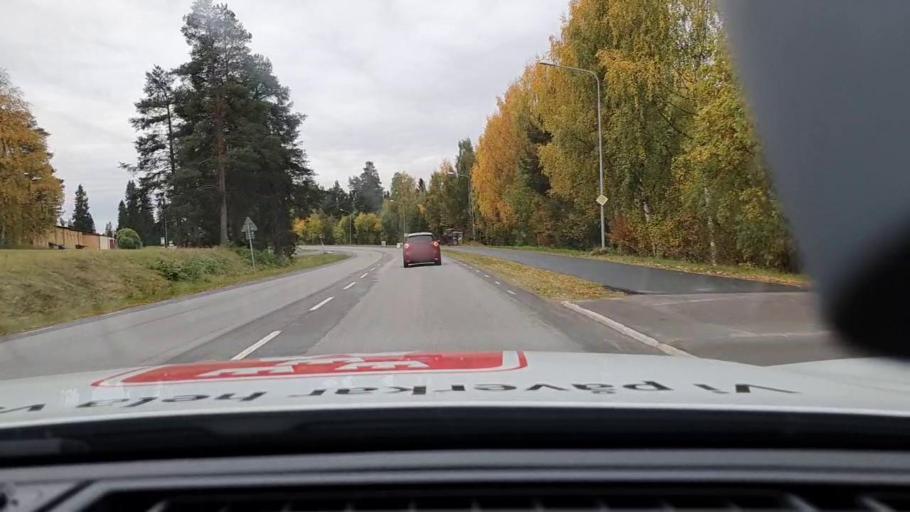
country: SE
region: Norrbotten
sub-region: Bodens Kommun
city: Boden
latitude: 65.8133
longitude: 21.6781
